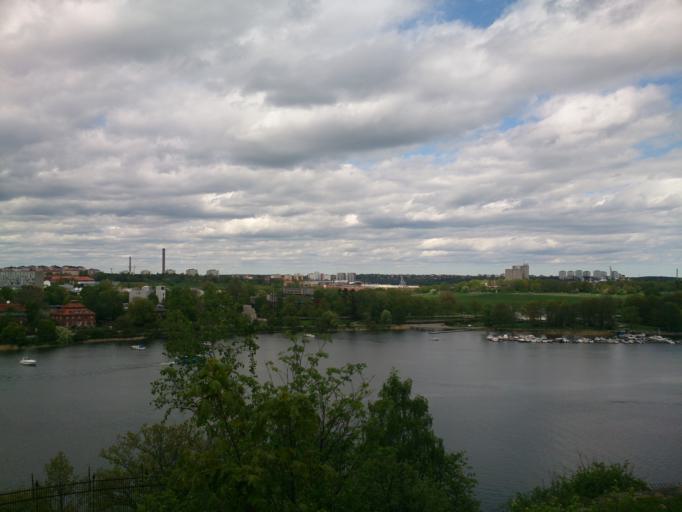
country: SE
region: Stockholm
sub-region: Stockholms Kommun
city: OEstermalm
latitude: 59.3287
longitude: 18.1066
